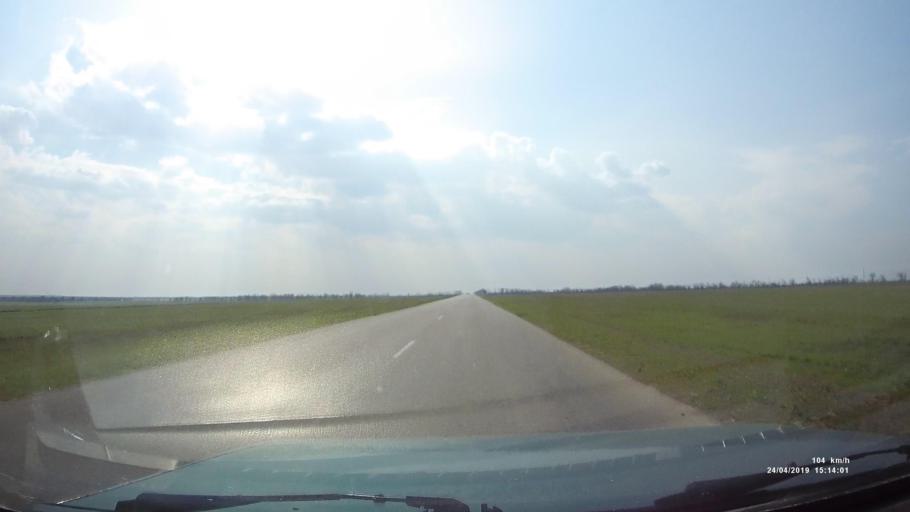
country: RU
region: Rostov
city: Remontnoye
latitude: 46.5465
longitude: 43.2670
